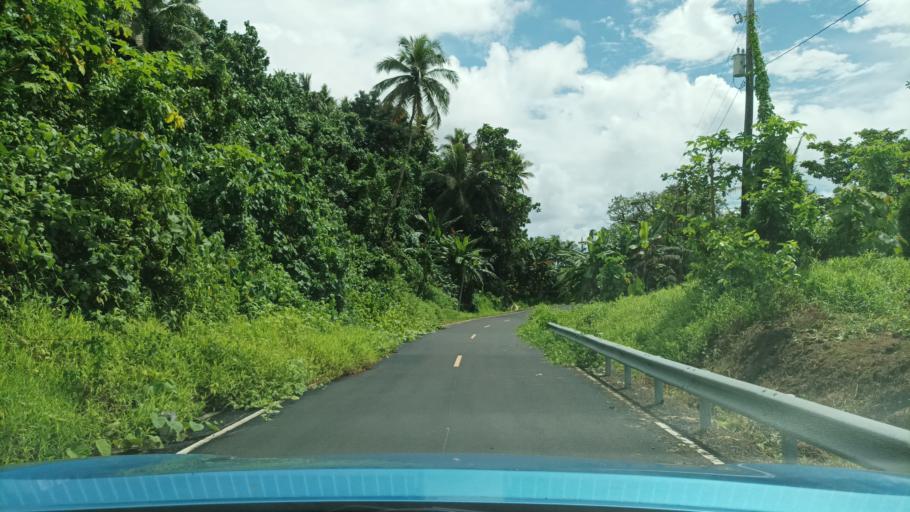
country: FM
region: Pohnpei
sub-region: Madolenihm Municipality
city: Madolenihm Municipality Government
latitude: 6.8636
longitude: 158.3254
